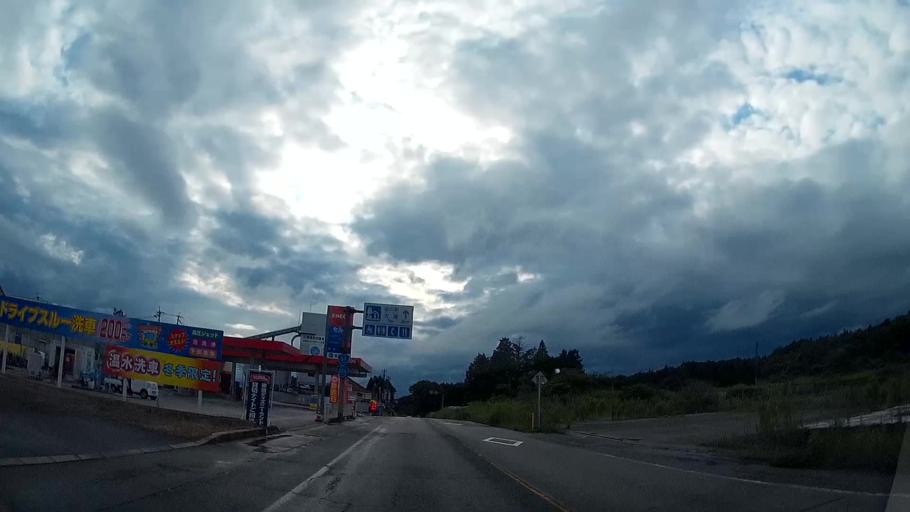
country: JP
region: Kumamoto
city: Ozu
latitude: 32.8788
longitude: 130.9128
